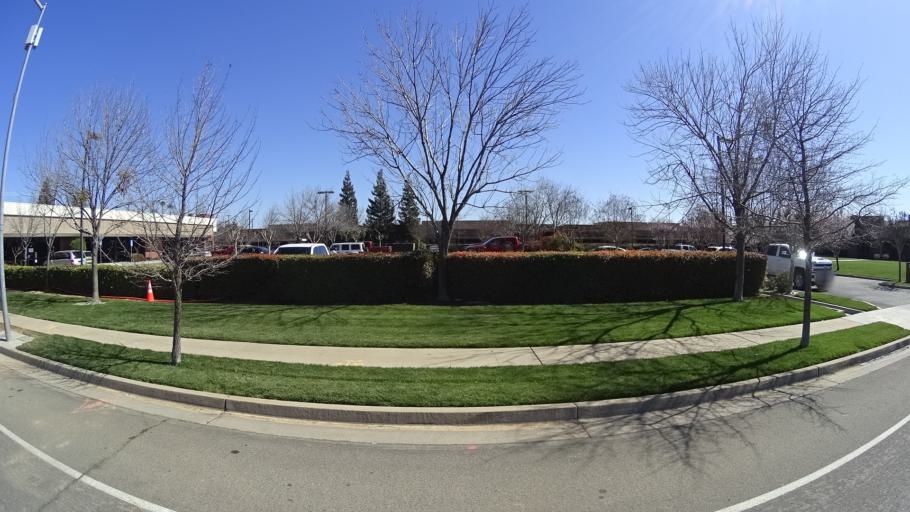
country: US
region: California
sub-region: Fresno County
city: Clovis
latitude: 36.8440
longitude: -119.7611
